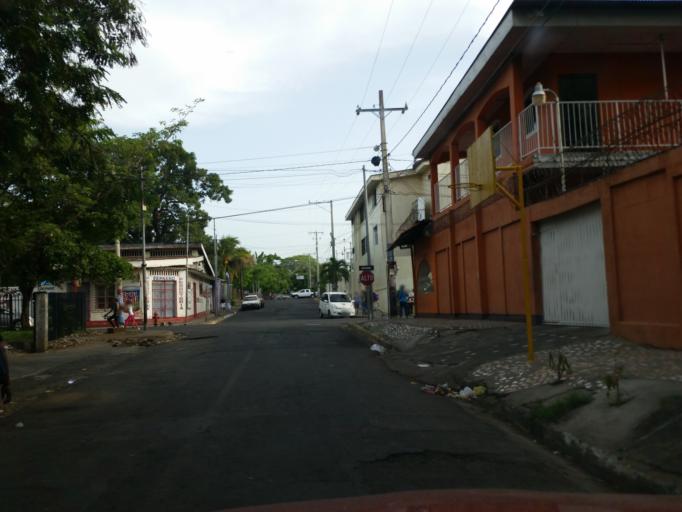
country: NI
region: Managua
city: Managua
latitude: 12.1465
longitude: -86.2779
